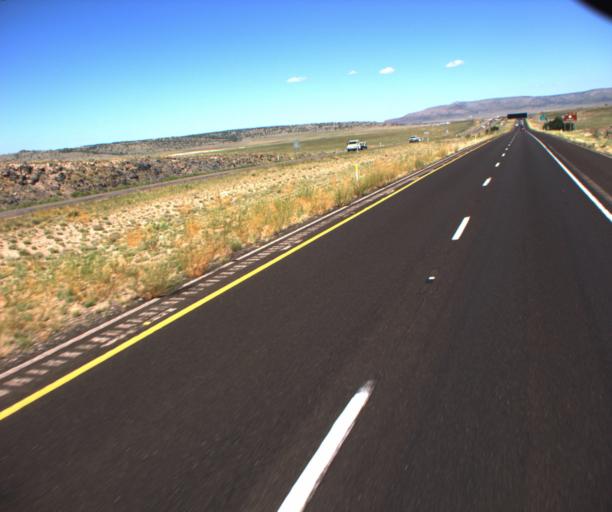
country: US
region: Arizona
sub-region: Yavapai County
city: Paulden
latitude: 35.3035
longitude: -112.8436
